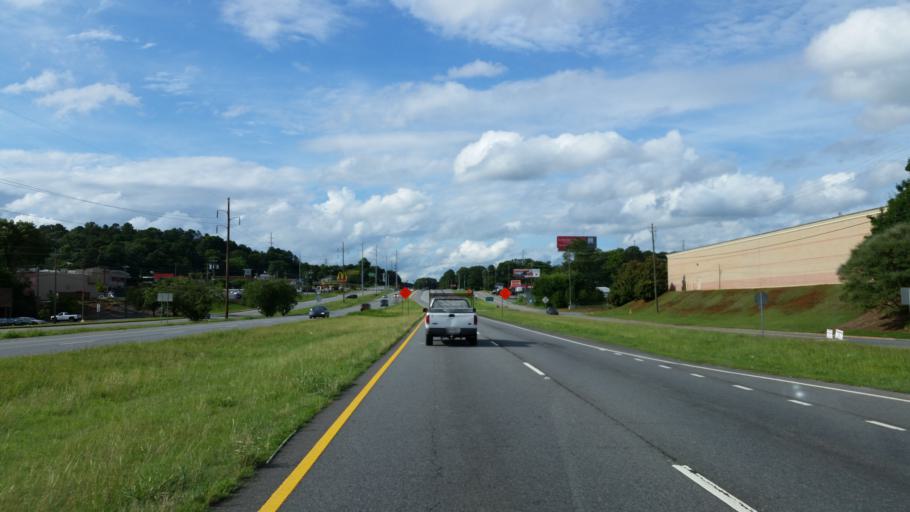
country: US
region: Georgia
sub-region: Bartow County
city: Cartersville
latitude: 34.1724
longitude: -84.7871
